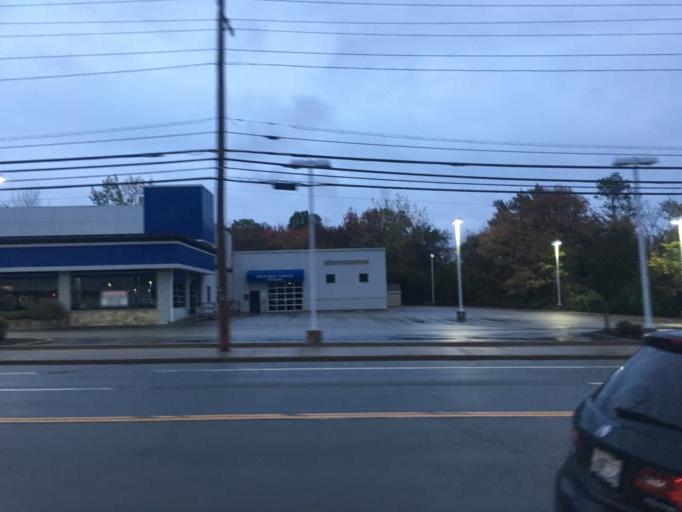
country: US
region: Rhode Island
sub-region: Kent County
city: West Warwick
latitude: 41.6727
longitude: -71.4998
